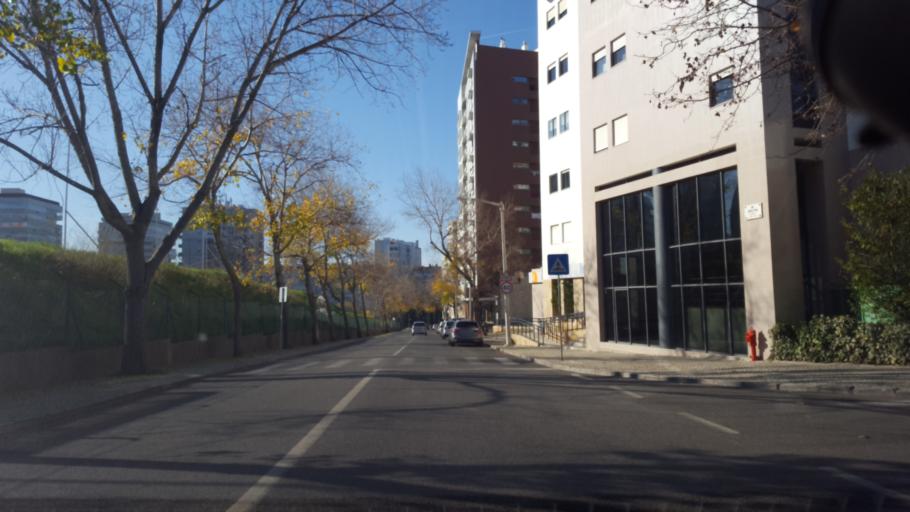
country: PT
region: Lisbon
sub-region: Odivelas
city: Pontinha
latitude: 38.7494
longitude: -9.1843
